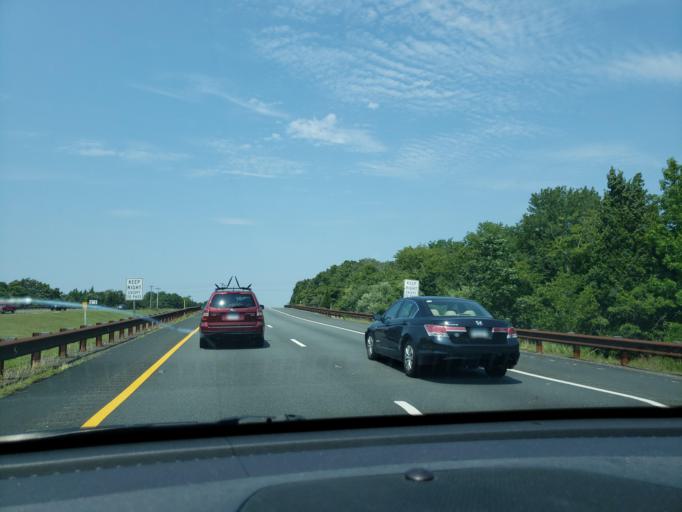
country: US
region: New Jersey
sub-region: Atlantic County
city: Somers Point
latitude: 39.3125
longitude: -74.6201
